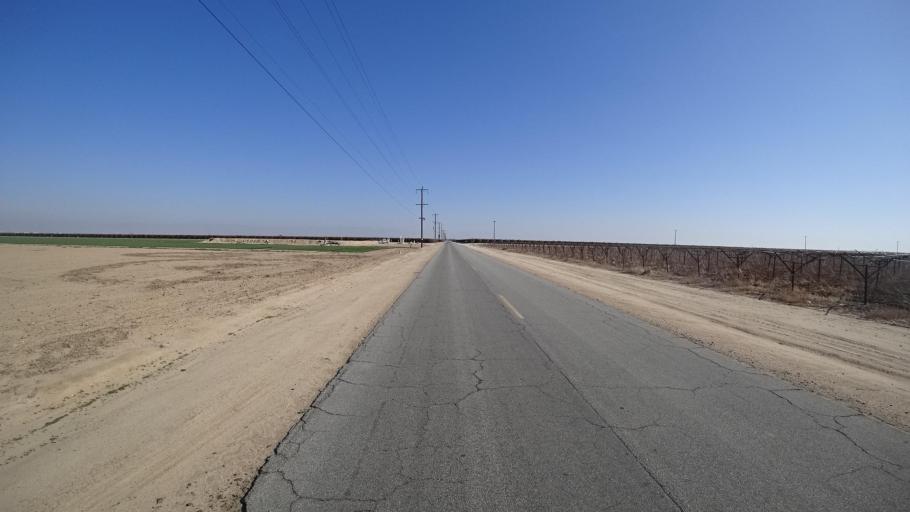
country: US
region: California
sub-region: Kern County
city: McFarland
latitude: 35.7035
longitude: -119.1800
